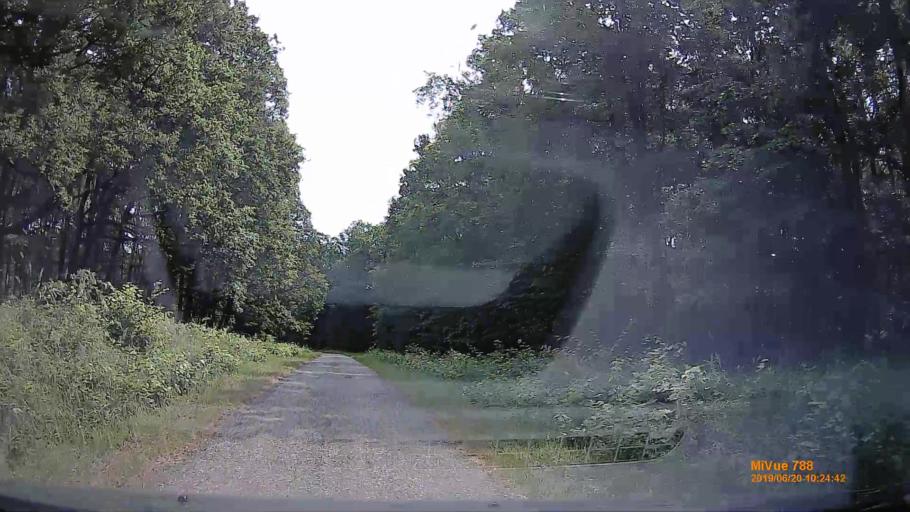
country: HU
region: Baranya
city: Mecseknadasd
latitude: 46.2099
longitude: 18.4830
